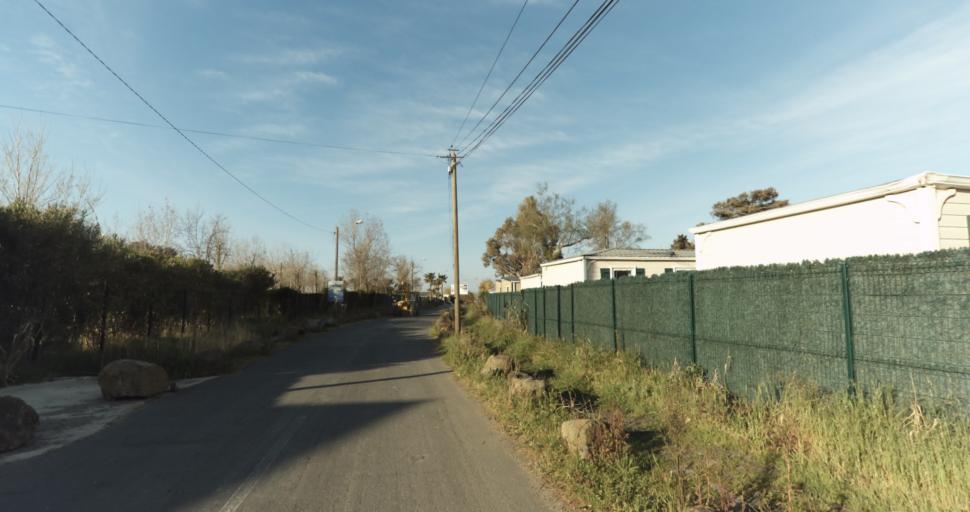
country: FR
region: Languedoc-Roussillon
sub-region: Departement de l'Herault
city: Le Cap d'Agde
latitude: 43.3065
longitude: 3.5392
